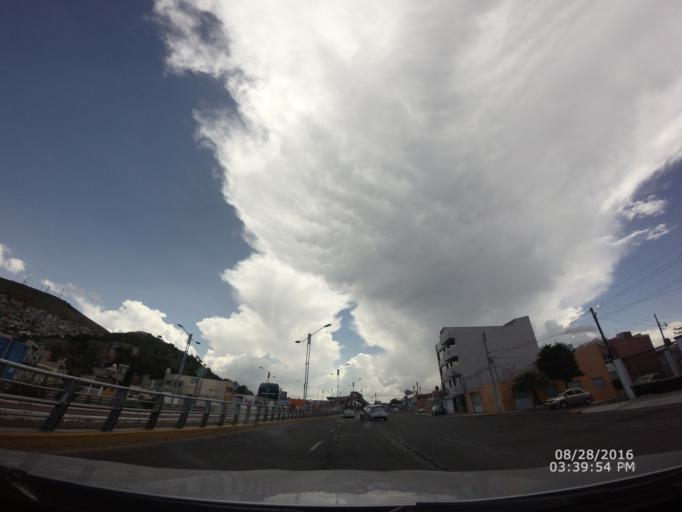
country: MX
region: Hidalgo
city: Pachuca de Soto
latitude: 20.1161
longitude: -98.7374
